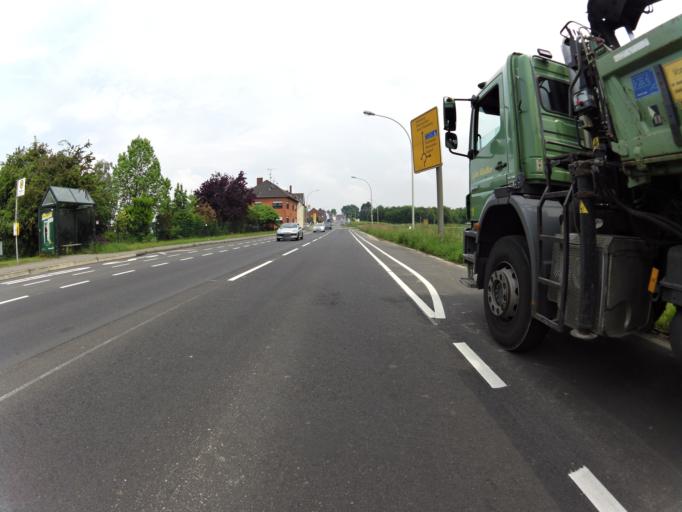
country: DE
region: North Rhine-Westphalia
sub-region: Regierungsbezirk Koln
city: Alsdorf
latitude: 50.8985
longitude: 6.1328
